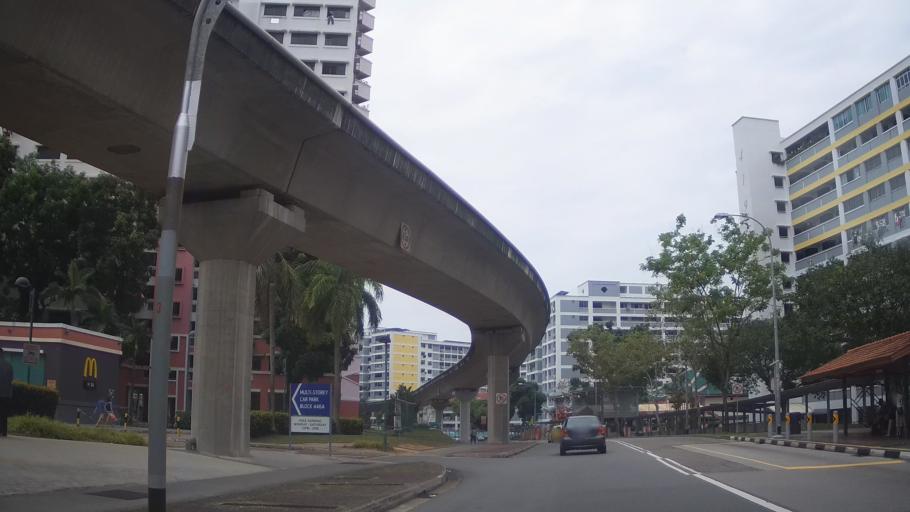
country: MY
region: Johor
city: Johor Bahru
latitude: 1.3842
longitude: 103.7704
